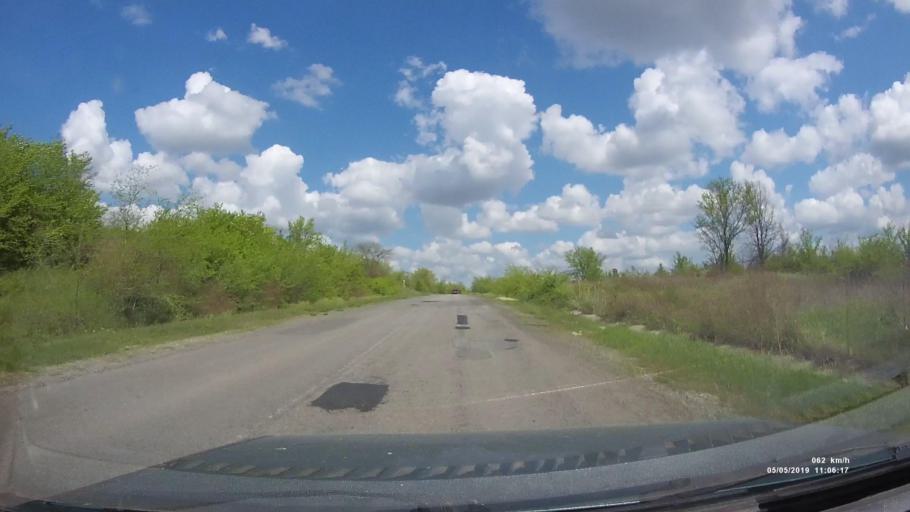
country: RU
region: Rostov
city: Ust'-Donetskiy
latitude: 47.7140
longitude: 40.9110
